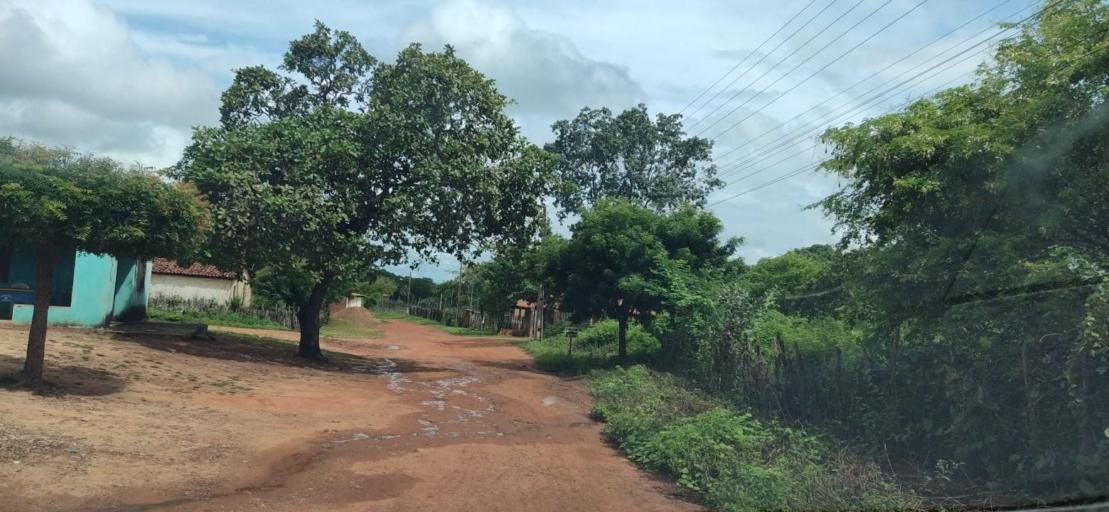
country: BR
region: Piaui
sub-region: Valenca Do Piaui
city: Valenca do Piaui
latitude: -6.1100
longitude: -41.7993
